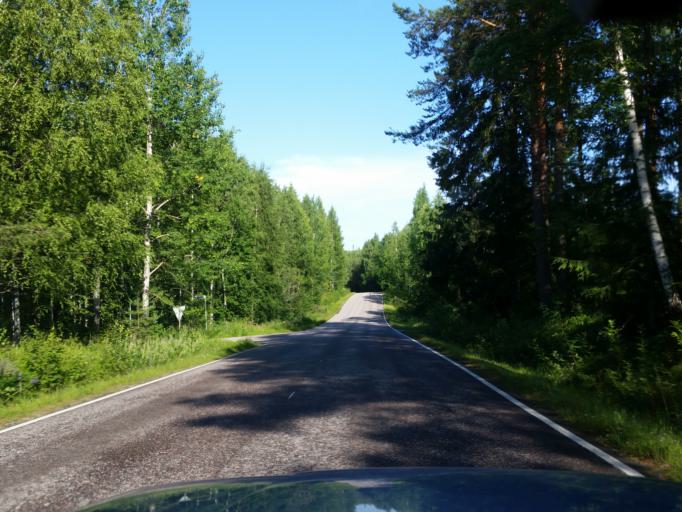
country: FI
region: Southern Savonia
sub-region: Savonlinna
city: Sulkava
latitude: 61.7926
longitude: 28.3862
